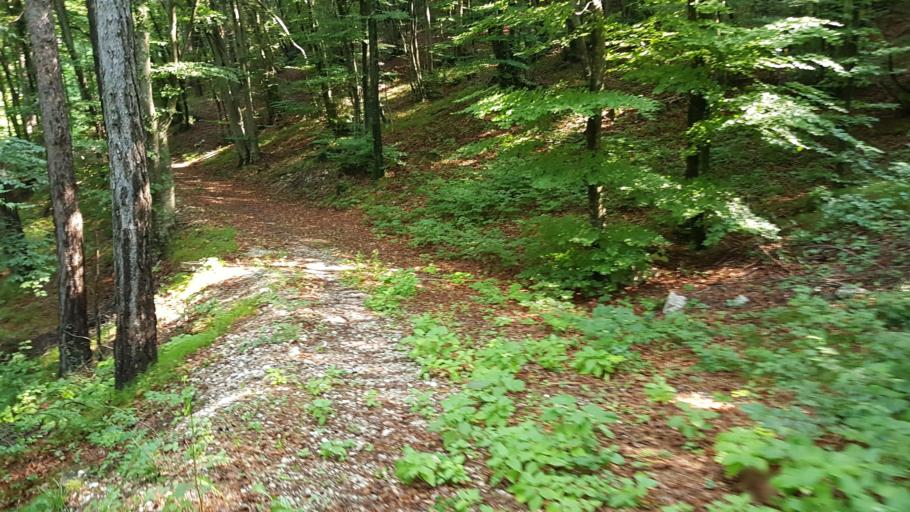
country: IT
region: Trentino-Alto Adige
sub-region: Provincia di Trento
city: Lasino
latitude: 46.0124
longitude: 10.9955
